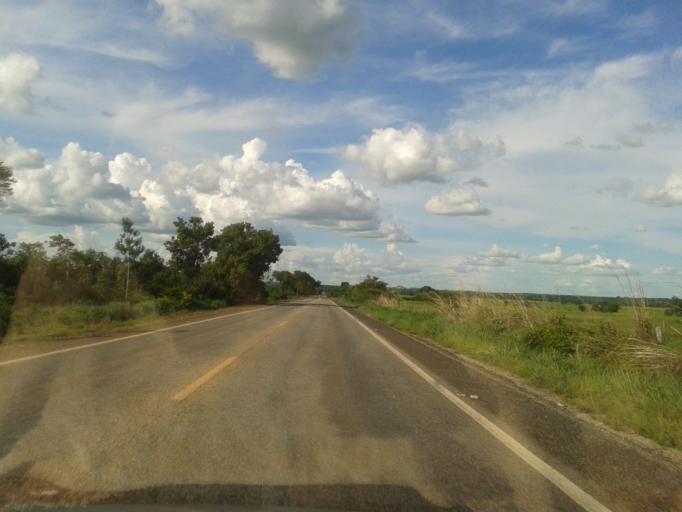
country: BR
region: Goias
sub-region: Mozarlandia
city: Mozarlandia
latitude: -14.5201
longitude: -50.4856
